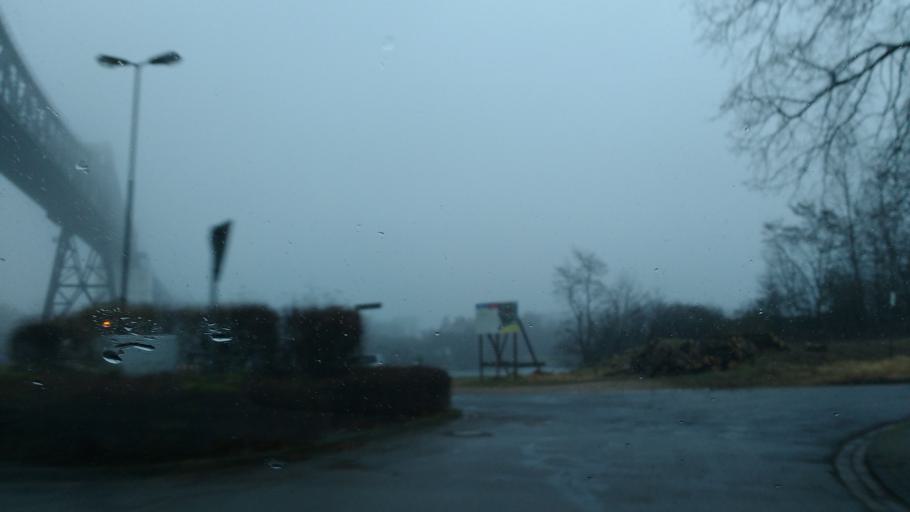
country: DE
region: Schleswig-Holstein
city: Osterronfeld
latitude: 54.2924
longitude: 9.6840
